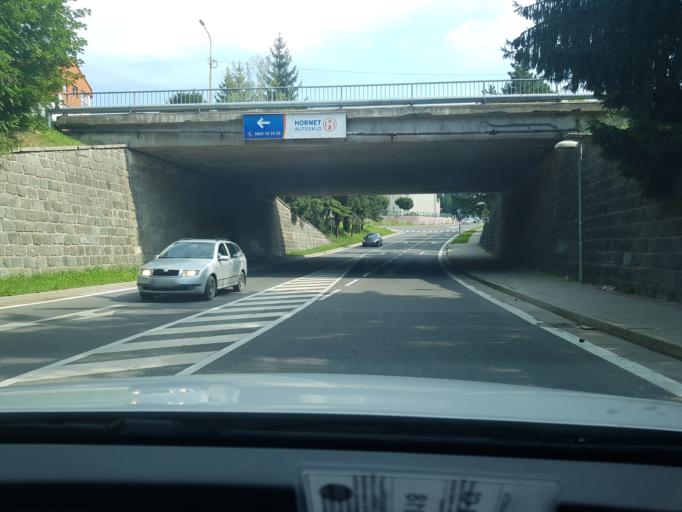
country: SK
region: Trenciansky
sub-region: Okres Povazska Bystrica
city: Povazska Bystrica
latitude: 49.1188
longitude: 18.4512
